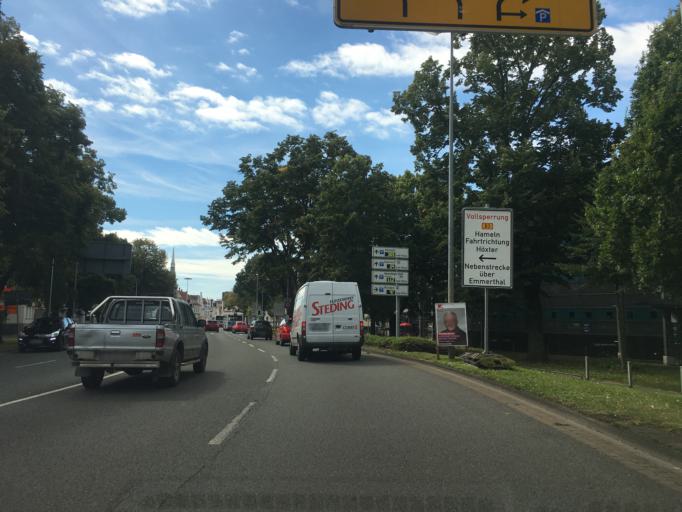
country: DE
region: Lower Saxony
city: Hameln
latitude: 52.1091
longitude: 9.3554
